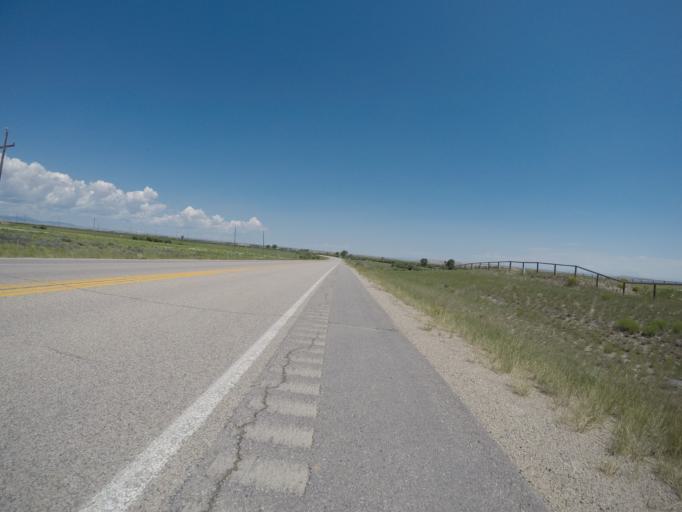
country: US
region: Wyoming
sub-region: Sublette County
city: Marbleton
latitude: 42.5143
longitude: -110.1049
